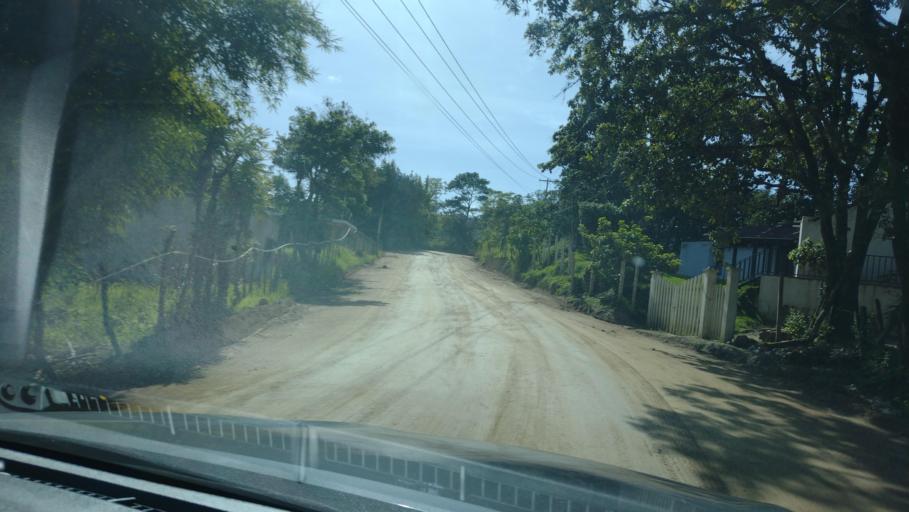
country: GT
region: Guatemala
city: Chinautla
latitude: 14.7611
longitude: -90.5234
